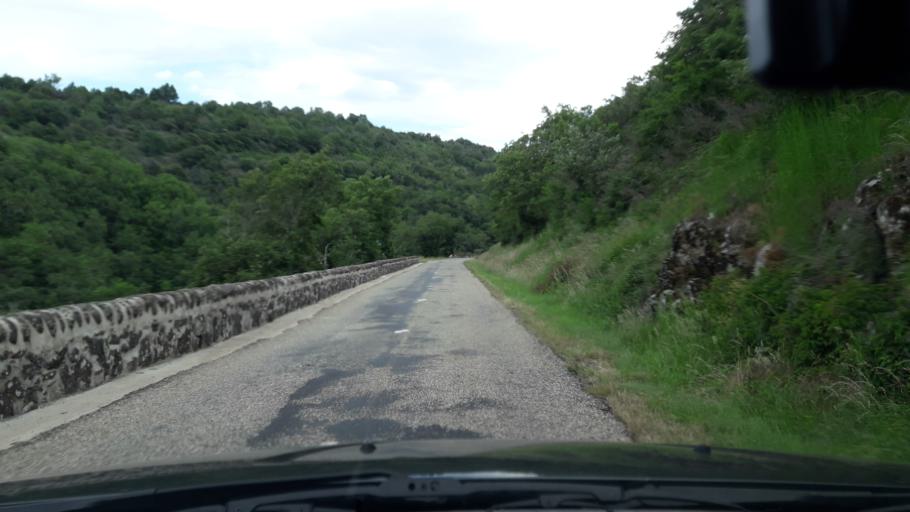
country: FR
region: Rhone-Alpes
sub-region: Departement de l'Ardeche
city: Saint-Priest
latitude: 44.6607
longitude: 4.5300
